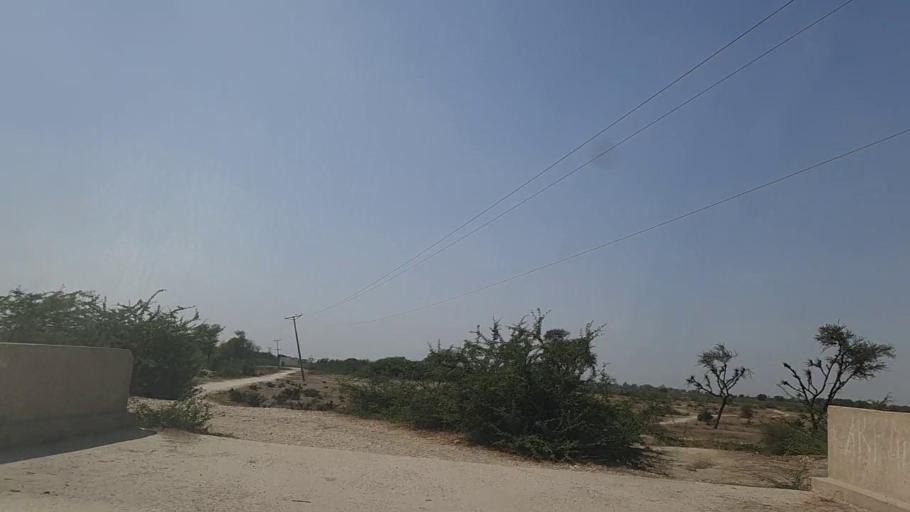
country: PK
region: Sindh
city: Naukot
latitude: 24.6517
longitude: 69.2772
